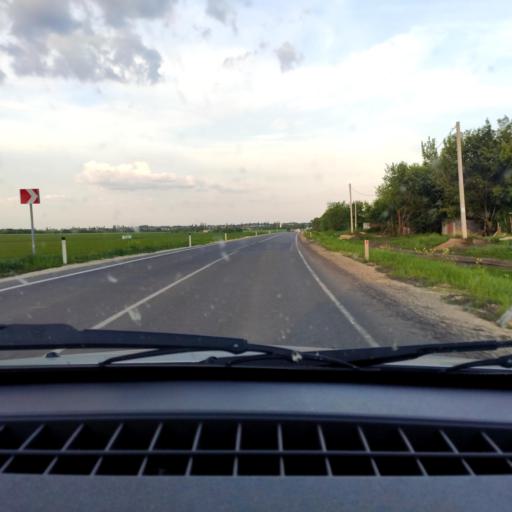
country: RU
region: Voronezj
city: Ramon'
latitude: 51.9228
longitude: 39.2981
